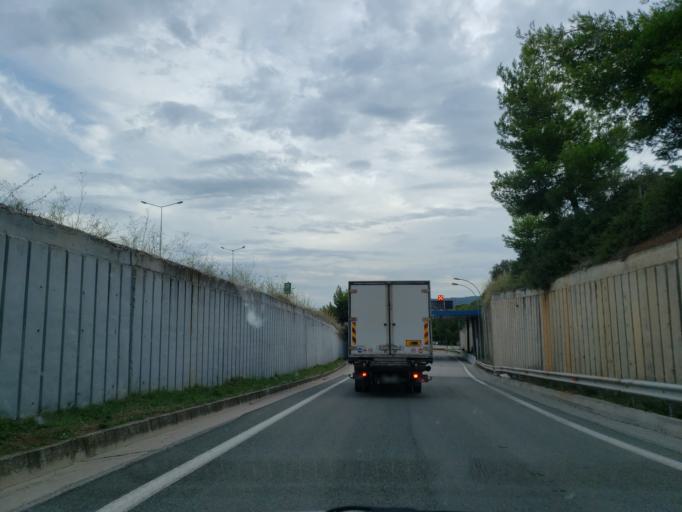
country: GR
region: Attica
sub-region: Nomarchia Anatolikis Attikis
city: Afidnes
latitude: 38.2032
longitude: 23.8542
